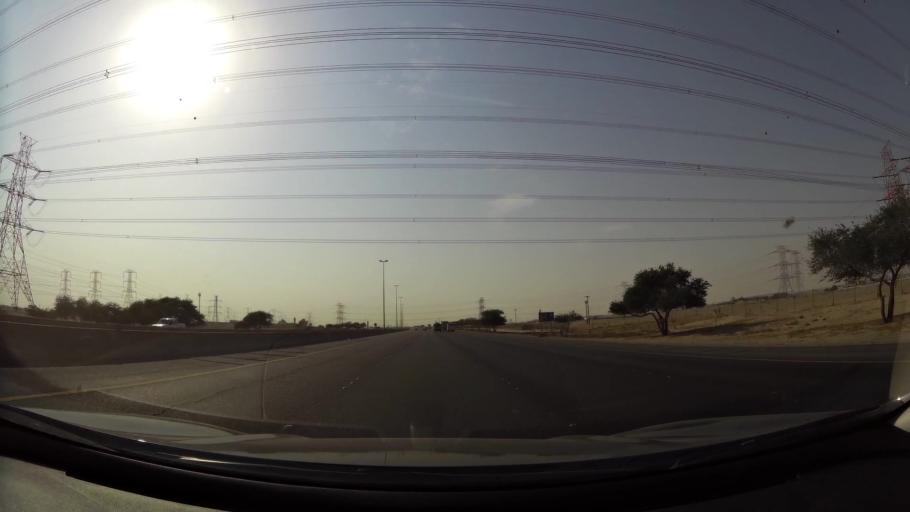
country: KW
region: Al Ahmadi
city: Al Ahmadi
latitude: 29.0117
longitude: 48.0931
